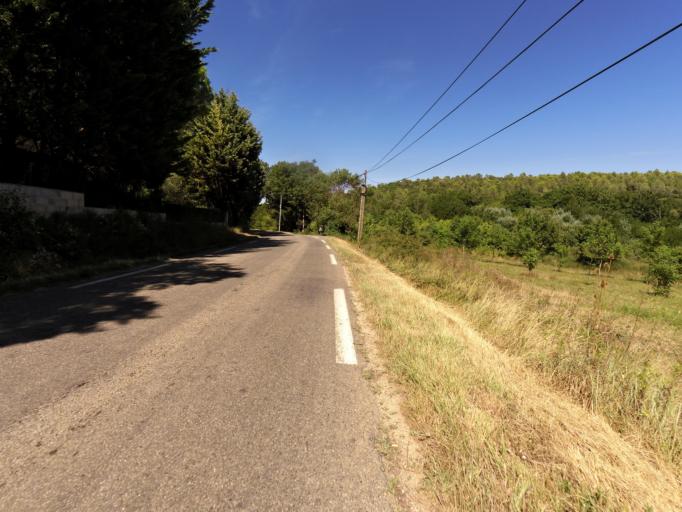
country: FR
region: Languedoc-Roussillon
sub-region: Departement du Gard
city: Sommieres
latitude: 43.8181
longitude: 4.0692
